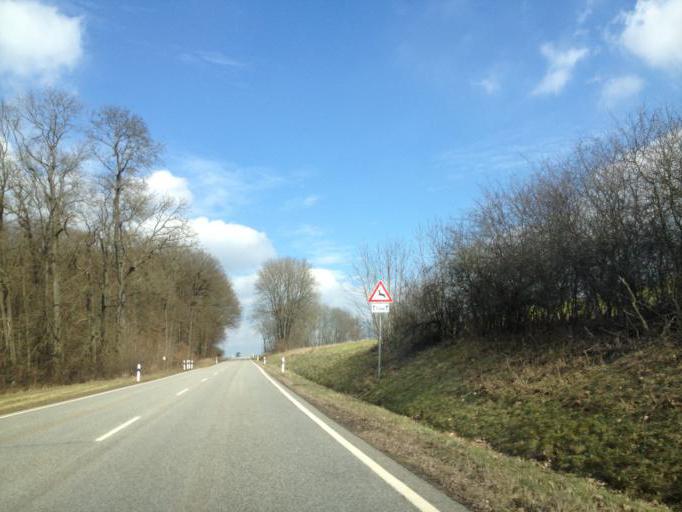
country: DE
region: Rheinland-Pfalz
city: Selchenbach
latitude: 49.5043
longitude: 7.3002
